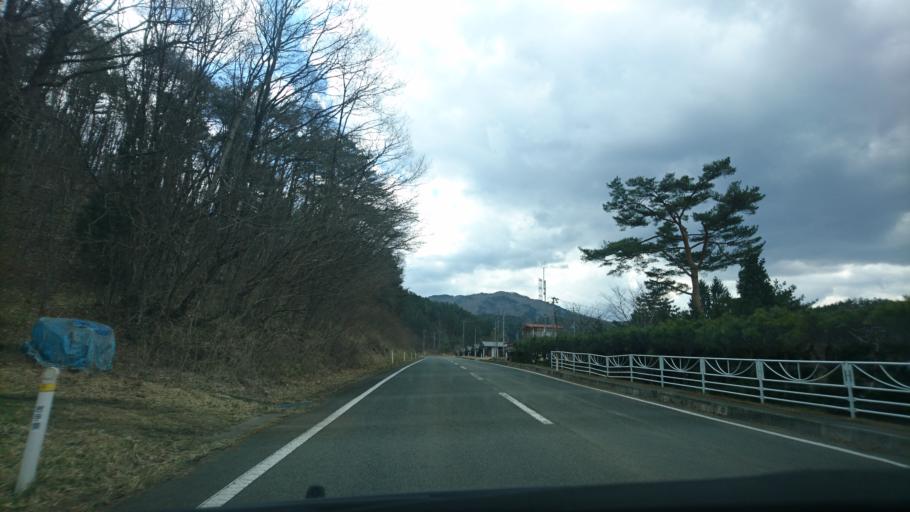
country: JP
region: Iwate
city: Tono
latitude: 39.3517
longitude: 141.3436
